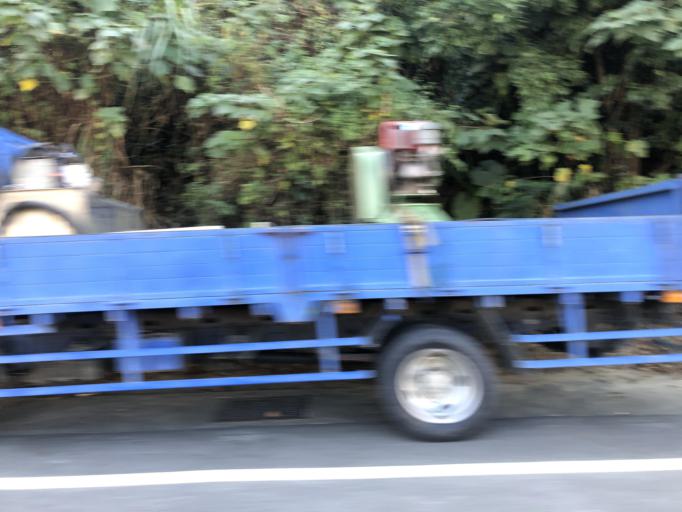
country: TW
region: Taiwan
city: Yujing
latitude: 23.0642
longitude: 120.3866
